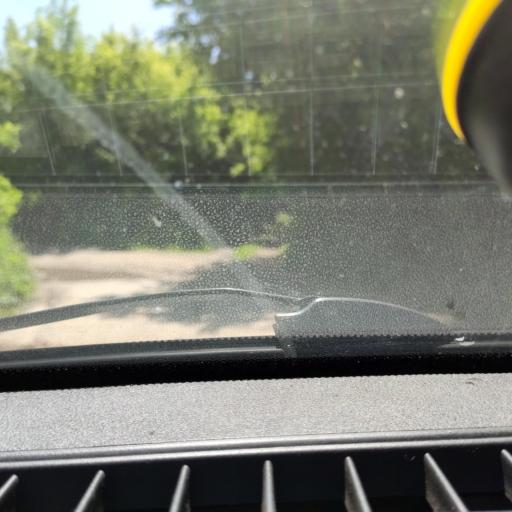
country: RU
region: Samara
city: Zhigulevsk
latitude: 53.3777
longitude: 49.5086
